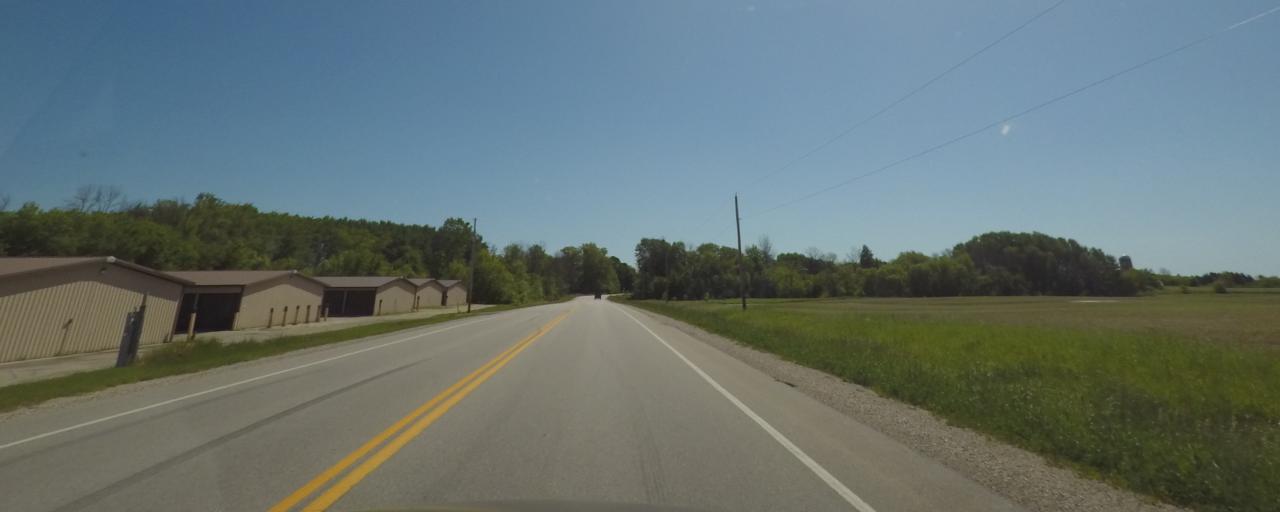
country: US
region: Wisconsin
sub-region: Sheboygan County
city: Plymouth
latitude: 43.7463
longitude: -87.9155
